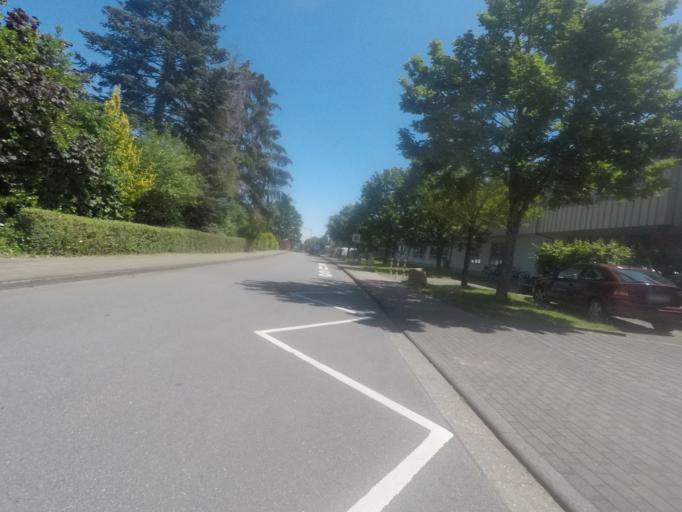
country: DE
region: North Rhine-Westphalia
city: Enger
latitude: 52.0932
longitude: 8.5323
